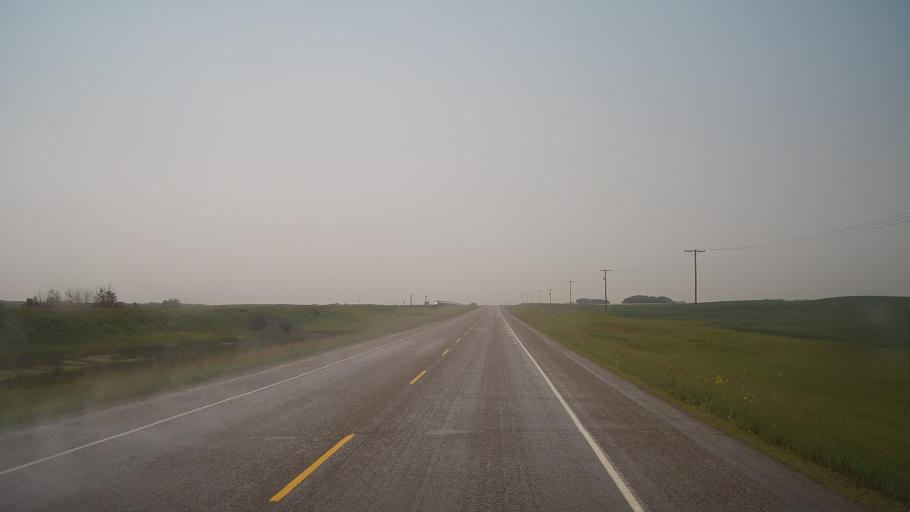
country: CA
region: Saskatchewan
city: Biggar
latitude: 52.1555
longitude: -108.2545
